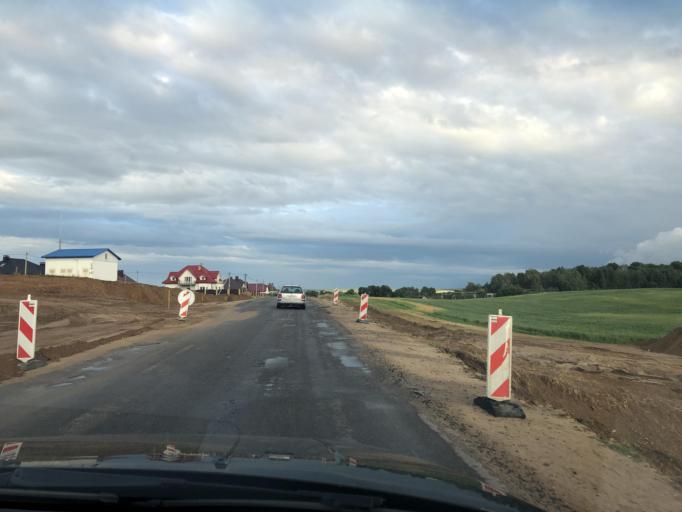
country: BY
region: Grodnenskaya
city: Hrodna
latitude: 53.7113
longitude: 23.8853
